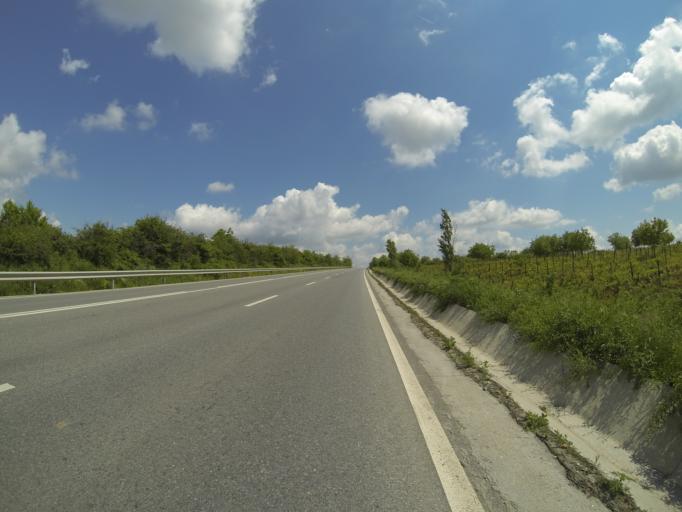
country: RO
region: Dolj
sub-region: Comuna Carcea
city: Carcea
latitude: 44.2657
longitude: 23.8929
